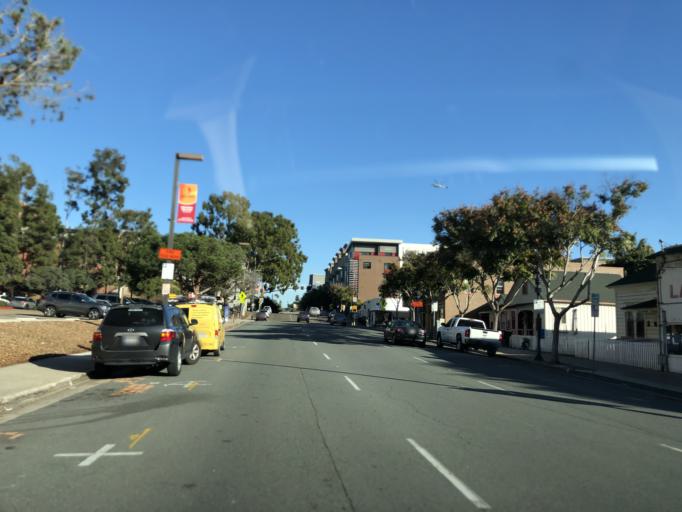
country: US
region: California
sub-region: San Diego County
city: San Diego
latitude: 32.7168
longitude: -117.1530
